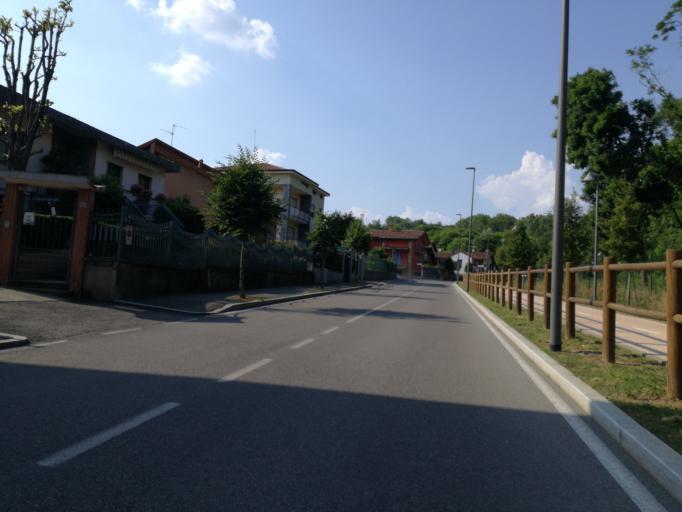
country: IT
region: Lombardy
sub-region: Provincia di Bergamo
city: Calusco d'Adda
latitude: 45.6951
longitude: 9.4670
